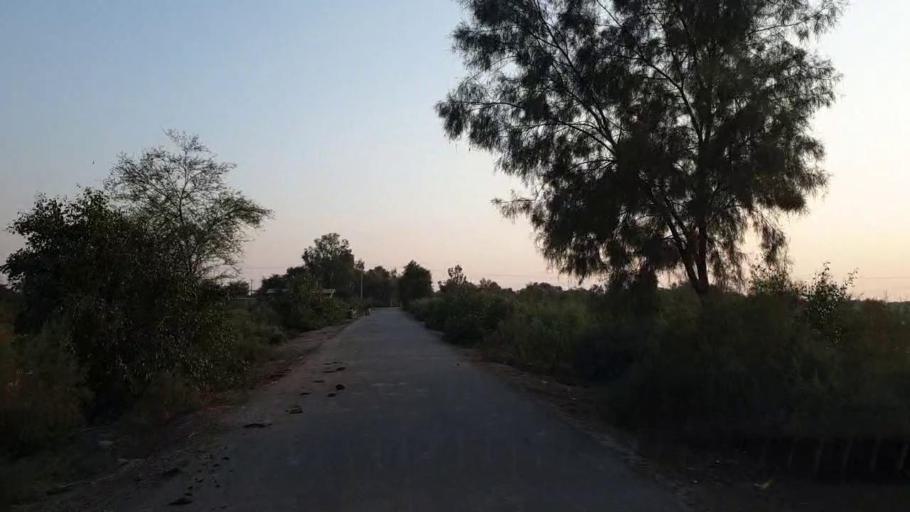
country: PK
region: Sindh
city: Sehwan
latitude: 26.4502
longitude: 67.7679
